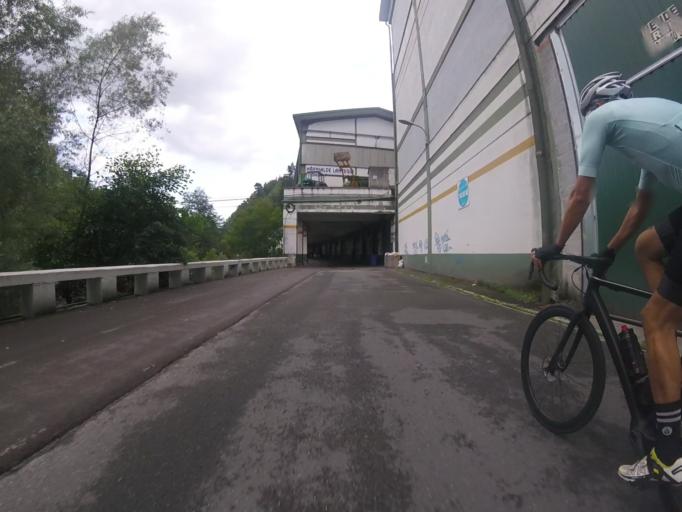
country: ES
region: Basque Country
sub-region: Provincia de Guipuzcoa
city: Alegria de Oria
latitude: 43.1181
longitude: -2.0901
